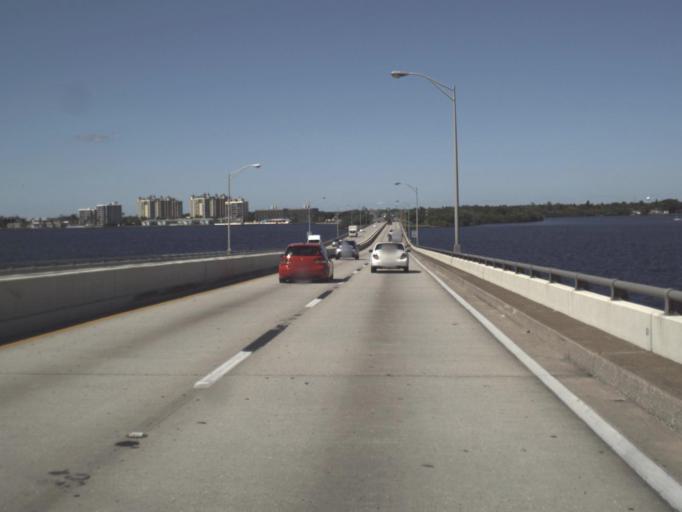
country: US
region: Florida
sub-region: Lee County
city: North Fort Myers
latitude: 26.6487
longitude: -81.8766
